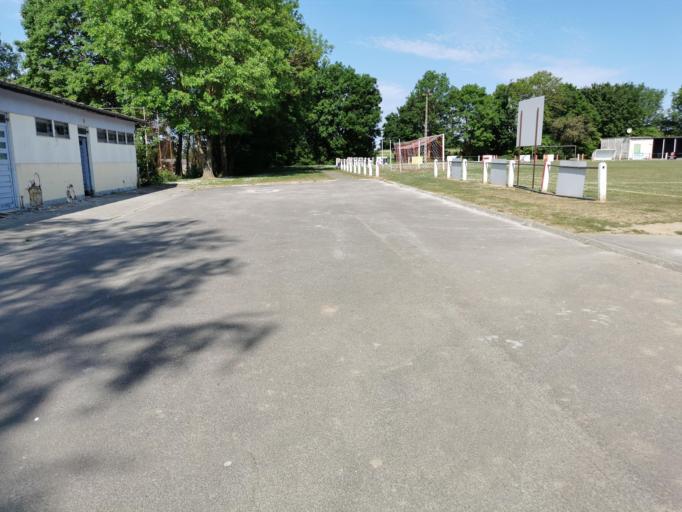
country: FR
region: Nord-Pas-de-Calais
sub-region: Departement du Nord
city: Marpent
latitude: 50.1789
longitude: 4.0897
